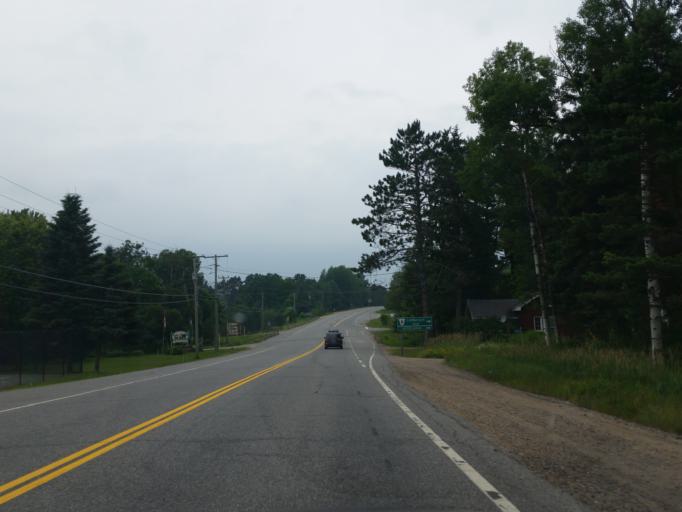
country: CA
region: Ontario
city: Huntsville
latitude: 45.3580
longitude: -79.0967
